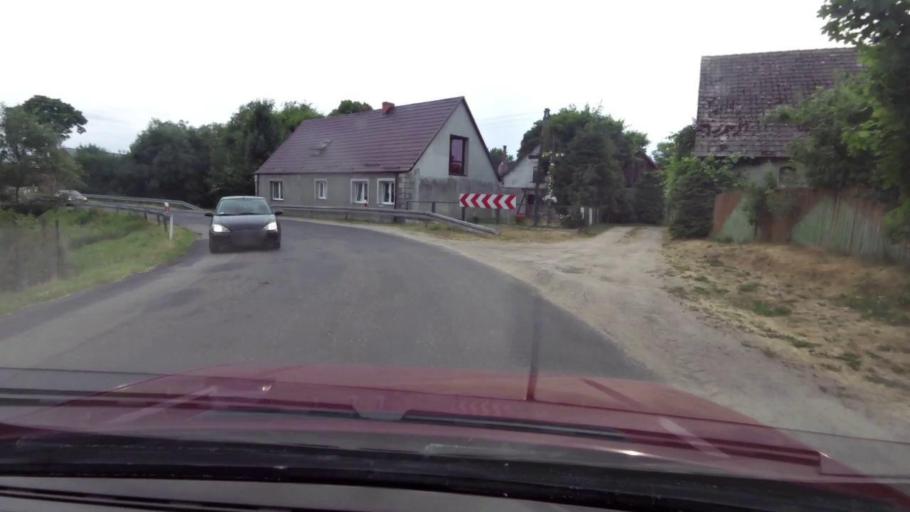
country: PL
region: Pomeranian Voivodeship
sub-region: Powiat bytowski
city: Trzebielino
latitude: 54.2655
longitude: 17.0590
